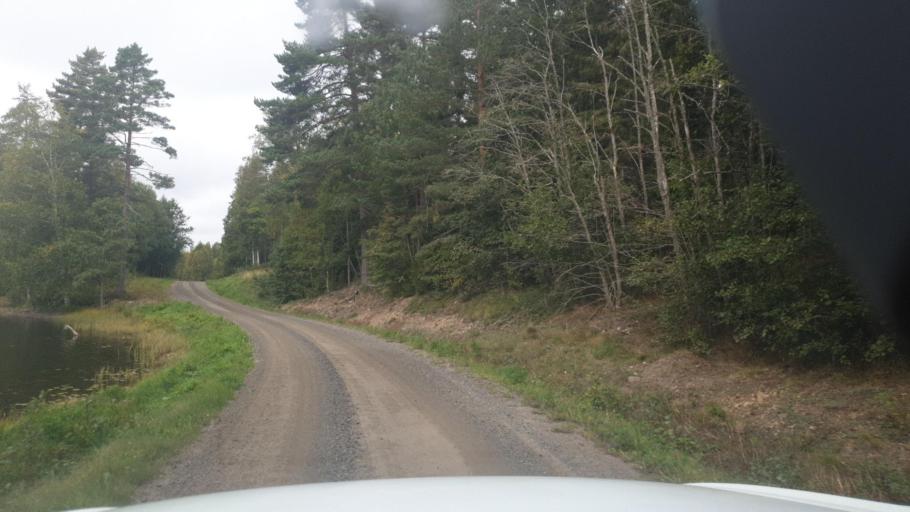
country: SE
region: Vaermland
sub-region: Arvika Kommun
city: Arvika
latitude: 59.8663
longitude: 12.8165
